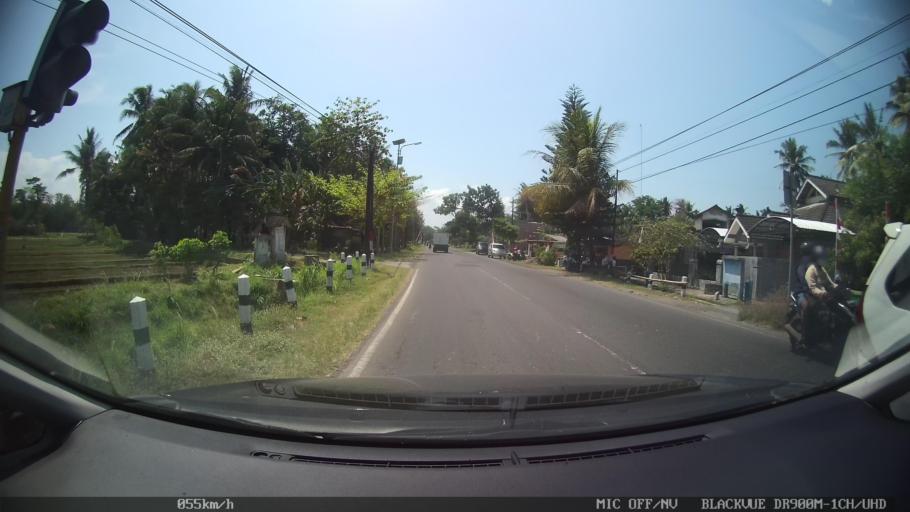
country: ID
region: Daerah Istimewa Yogyakarta
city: Srandakan
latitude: -7.9509
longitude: 110.2160
